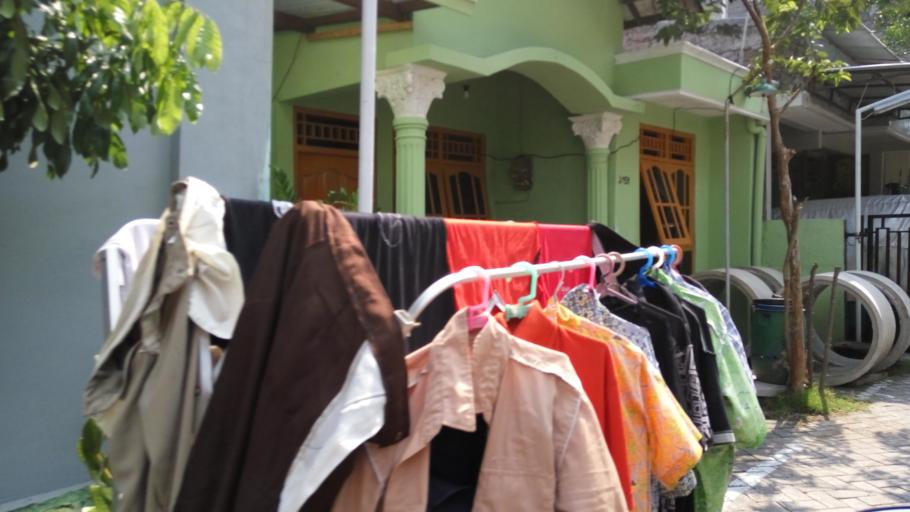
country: ID
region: Central Java
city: Mranggen
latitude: -7.0389
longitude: 110.4768
